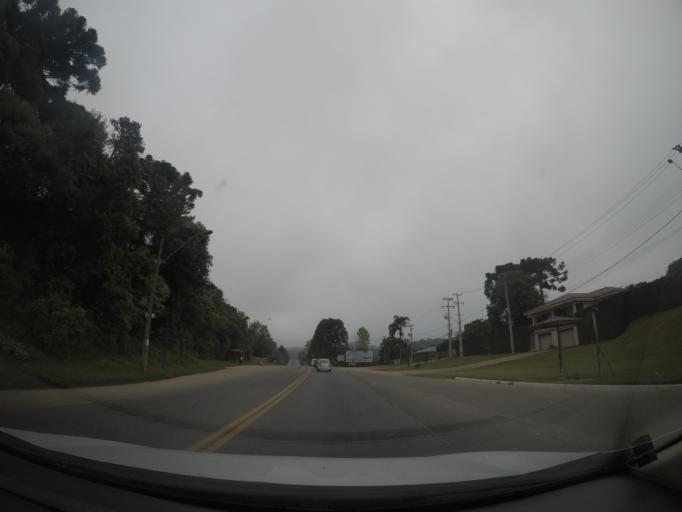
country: BR
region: Parana
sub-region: Almirante Tamandare
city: Almirante Tamandare
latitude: -25.3389
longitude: -49.2835
